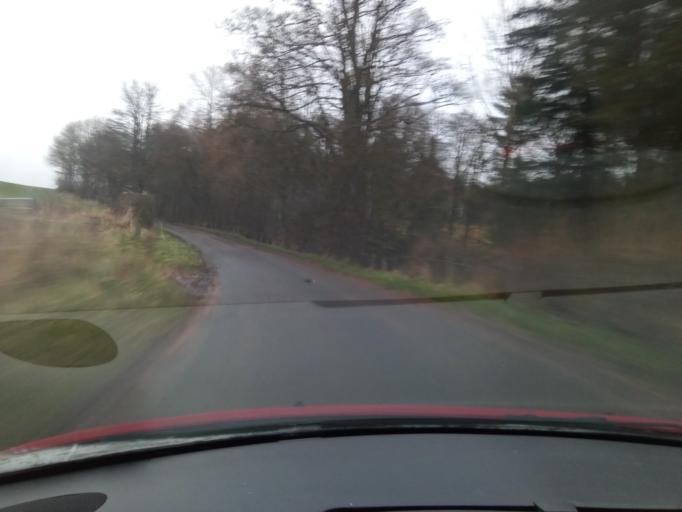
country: GB
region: Scotland
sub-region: The Scottish Borders
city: Kelso
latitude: 55.5418
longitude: -2.4371
